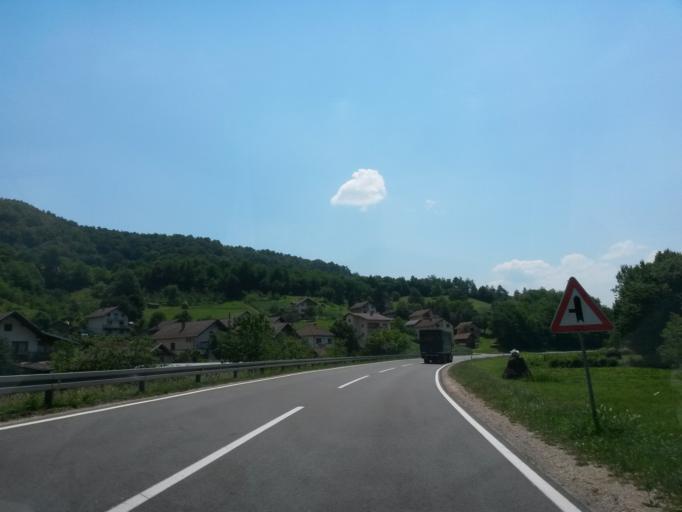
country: BA
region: Federation of Bosnia and Herzegovina
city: Lijesnica
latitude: 44.5091
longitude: 18.0820
